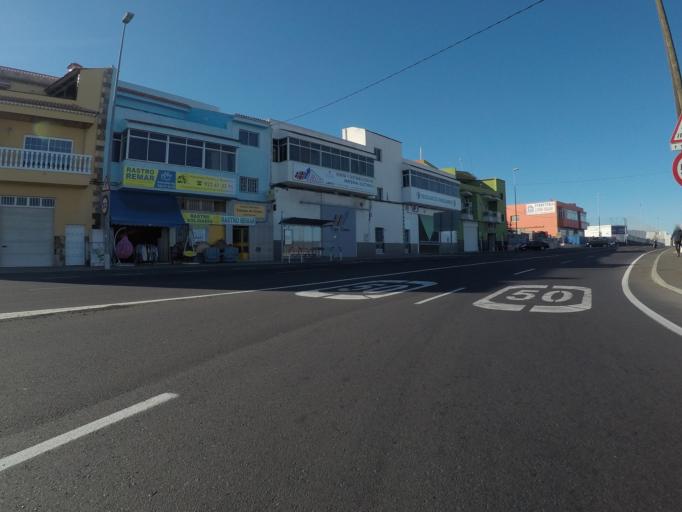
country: ES
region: Canary Islands
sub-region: Provincia de Santa Cruz de Tenerife
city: La Laguna
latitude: 28.4205
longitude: -16.3205
